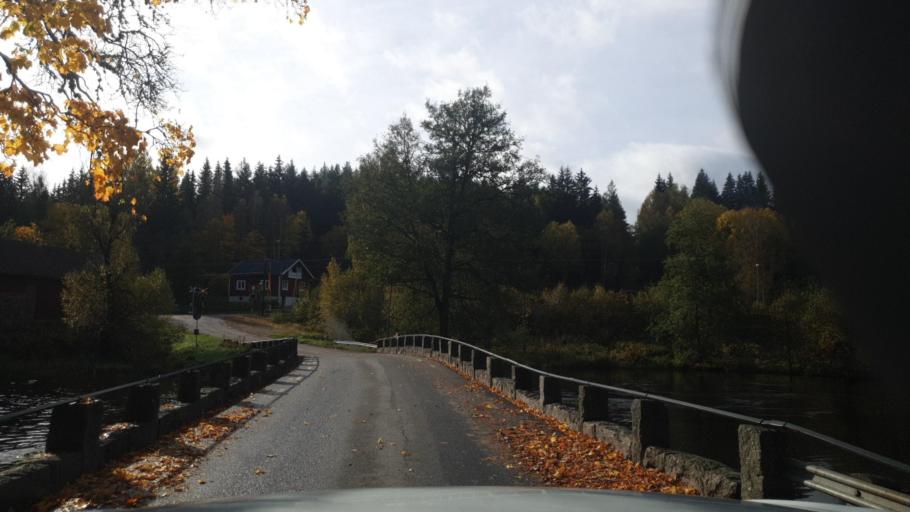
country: SE
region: Vaermland
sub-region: Sunne Kommun
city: Sunne
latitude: 59.6184
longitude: 12.9621
